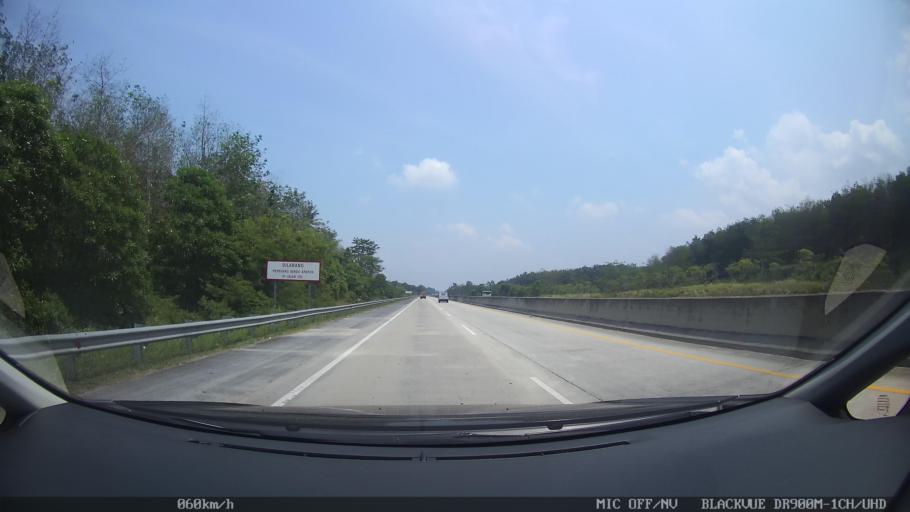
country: ID
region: Lampung
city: Kedaton
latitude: -5.3886
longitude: 105.3409
